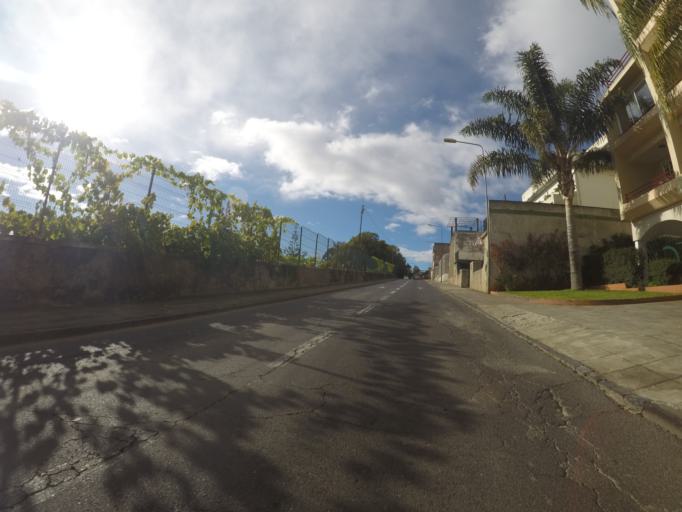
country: PT
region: Madeira
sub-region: Funchal
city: Funchal
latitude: 32.6437
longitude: -16.9263
